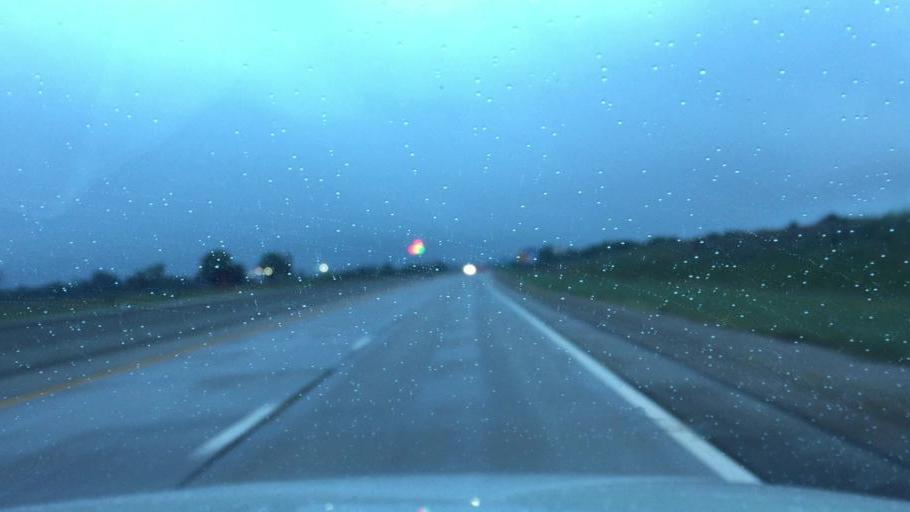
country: US
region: Kansas
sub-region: Neosho County
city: Chanute
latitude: 37.6594
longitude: -95.4796
